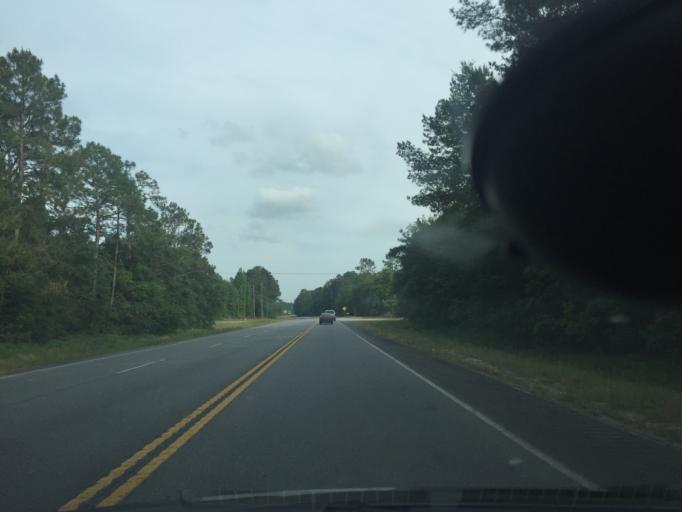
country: US
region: Georgia
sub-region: Chatham County
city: Bloomingdale
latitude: 32.0477
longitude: -81.3378
